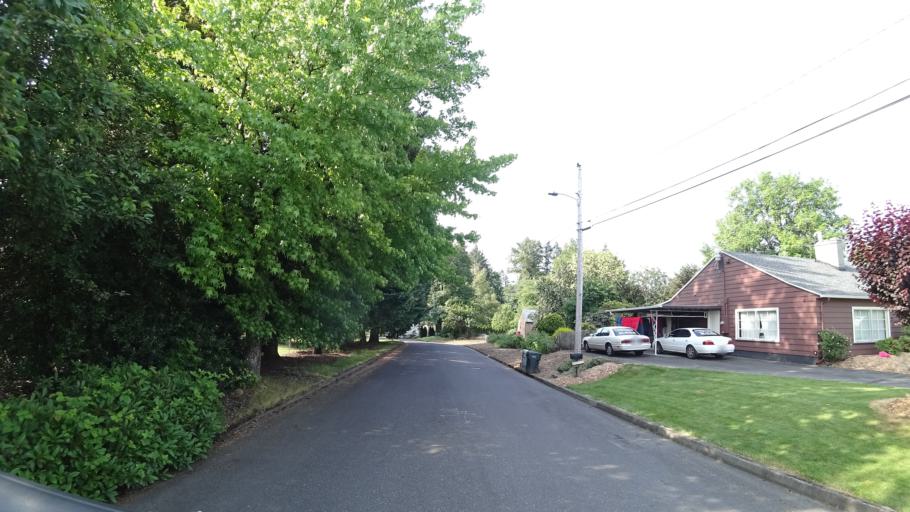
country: US
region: Oregon
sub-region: Clackamas County
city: Happy Valley
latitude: 45.4469
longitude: -122.5297
